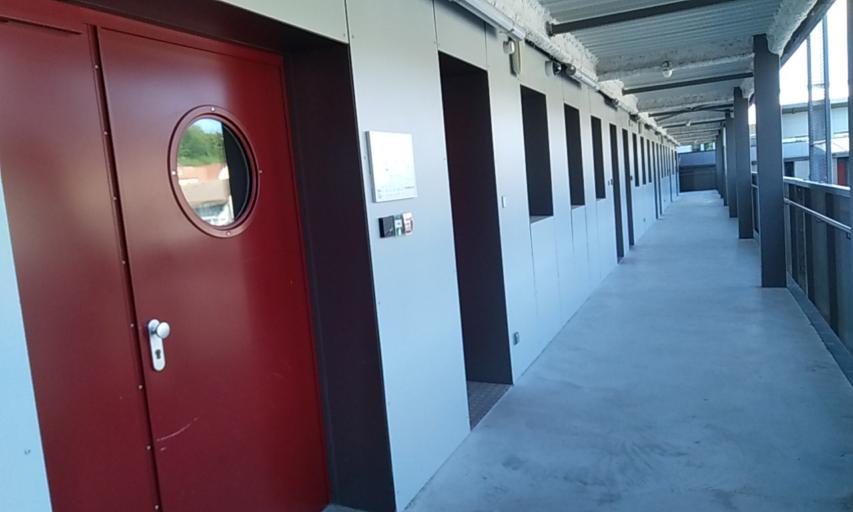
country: FR
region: Rhone-Alpes
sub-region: Departement de la Haute-Savoie
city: Annecy
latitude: 45.8913
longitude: 6.1222
